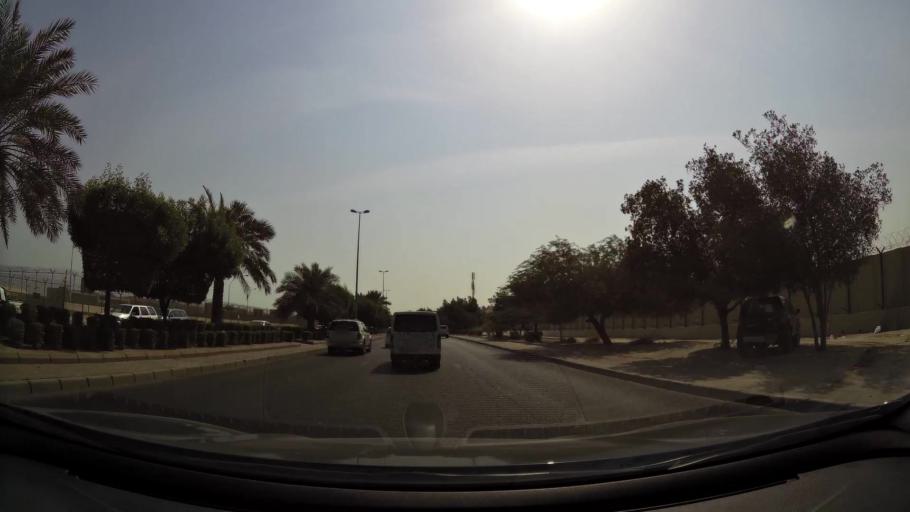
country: KW
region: Al Ahmadi
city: Al Manqaf
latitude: 29.1196
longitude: 48.1334
